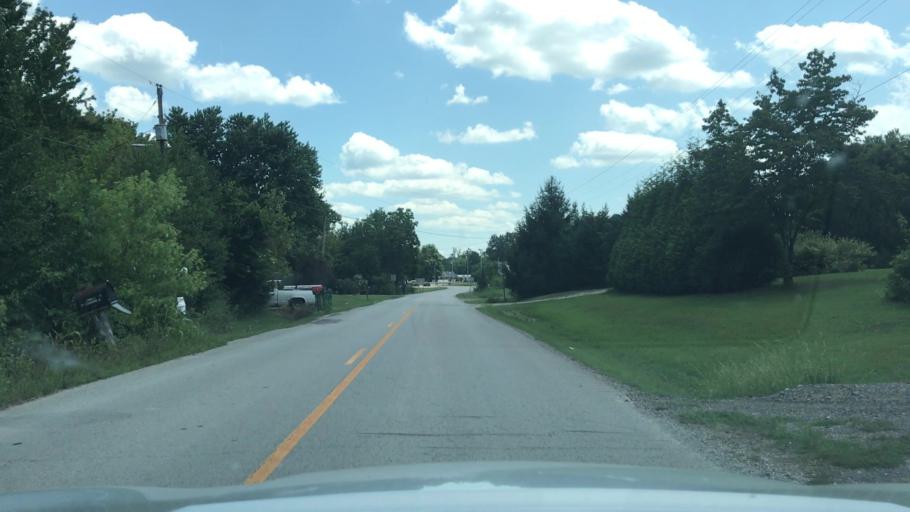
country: US
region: Kentucky
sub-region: Christian County
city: Hopkinsville
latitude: 36.9865
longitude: -87.3594
